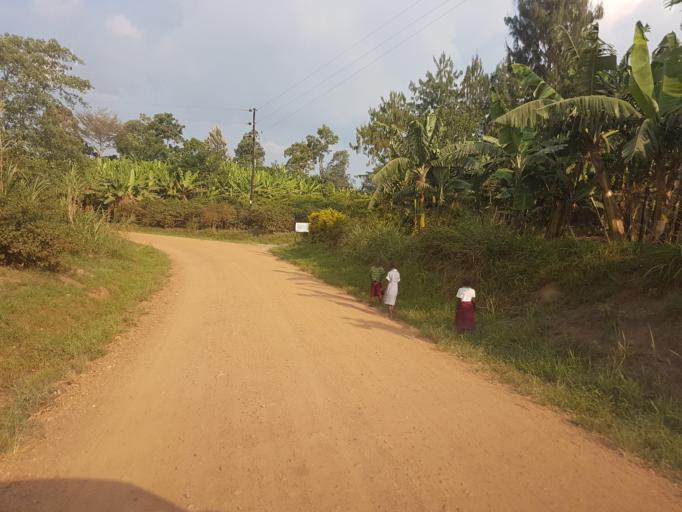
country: UG
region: Western Region
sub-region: Rukungiri District
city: Rukungiri
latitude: -0.6528
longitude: 29.8545
